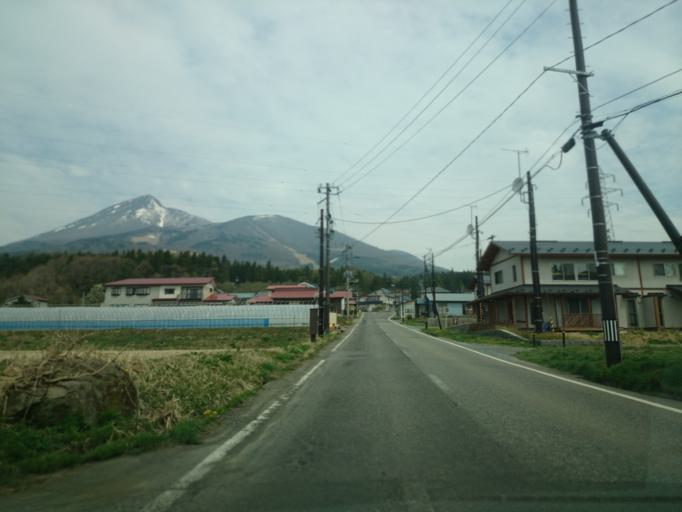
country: JP
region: Fukushima
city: Inawashiro
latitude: 37.5632
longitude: 140.0995
